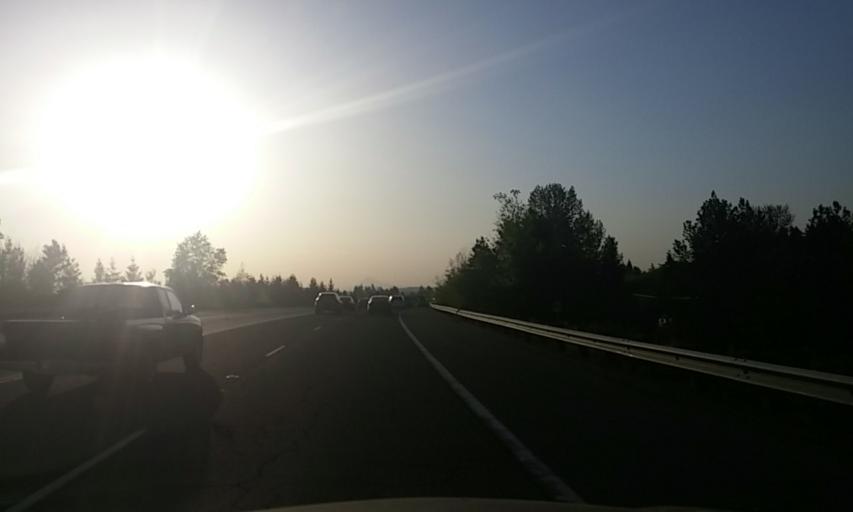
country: US
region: Oregon
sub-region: Washington County
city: Aloha
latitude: 45.4916
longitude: -122.8387
